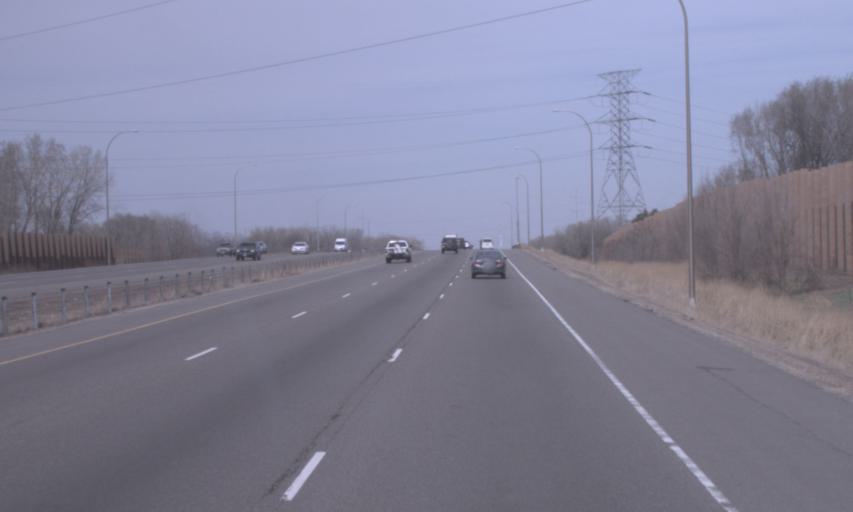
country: US
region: Minnesota
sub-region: Anoka County
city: Coon Rapids
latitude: 45.1674
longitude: -93.2904
